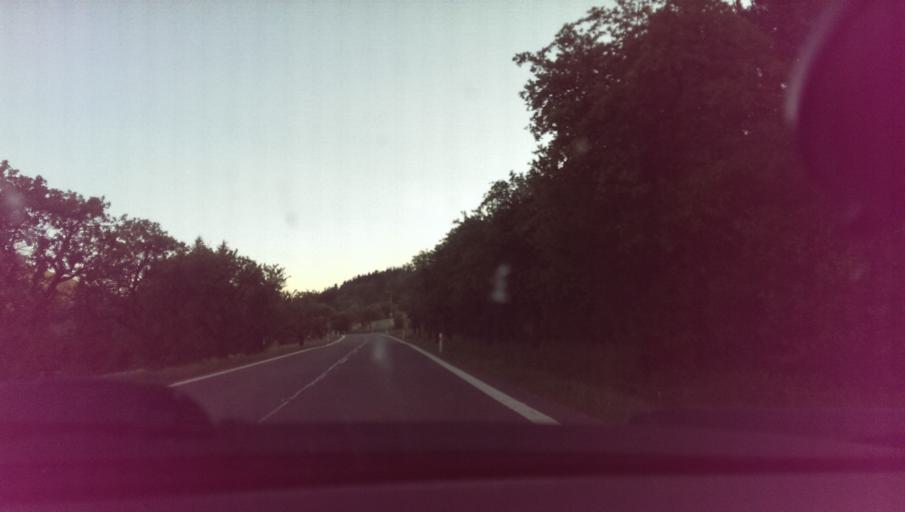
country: CZ
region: Moravskoslezsky
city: Frenstat pod Radhostem
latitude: 49.5171
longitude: 18.1982
